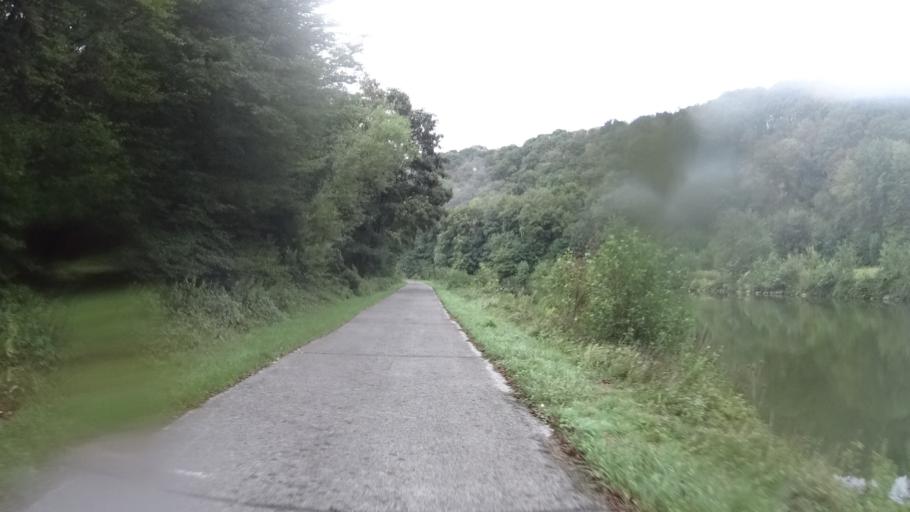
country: BE
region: Wallonia
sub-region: Province du Hainaut
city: Thuin
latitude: 50.3454
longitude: 4.3015
